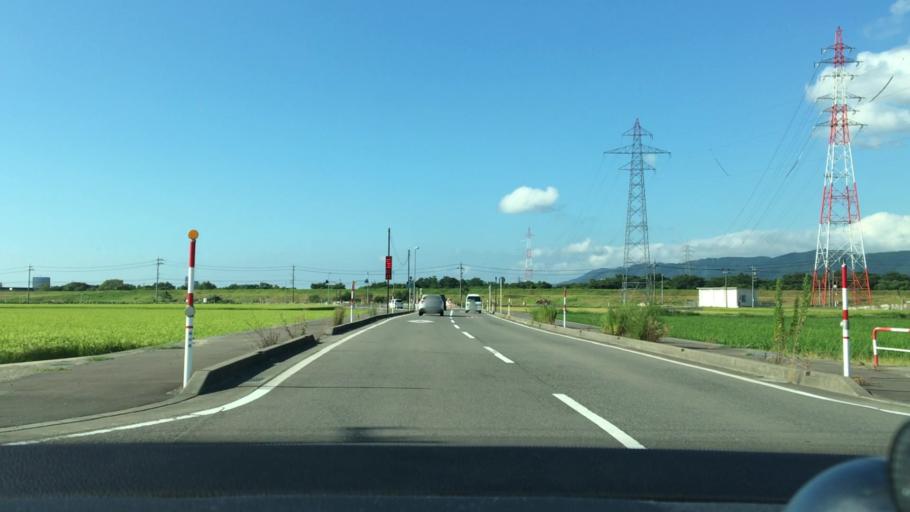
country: JP
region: Fukui
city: Maruoka
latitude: 36.0941
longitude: 136.2818
